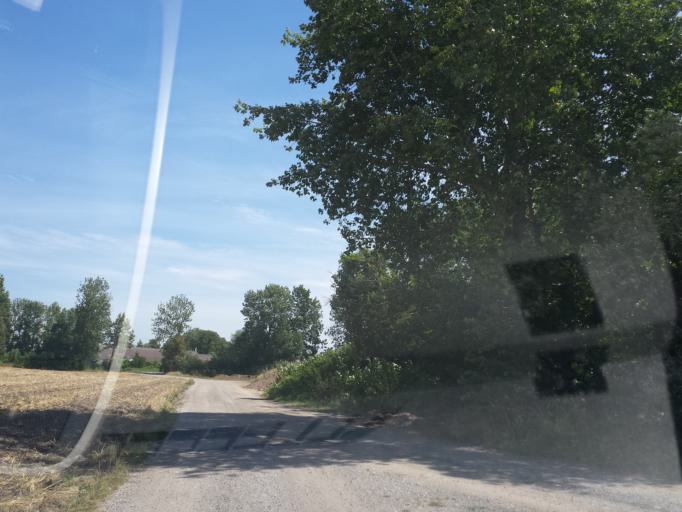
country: AT
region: Lower Austria
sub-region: Politischer Bezirk Neunkirchen
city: Enzenreith
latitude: 47.6765
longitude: 15.9614
